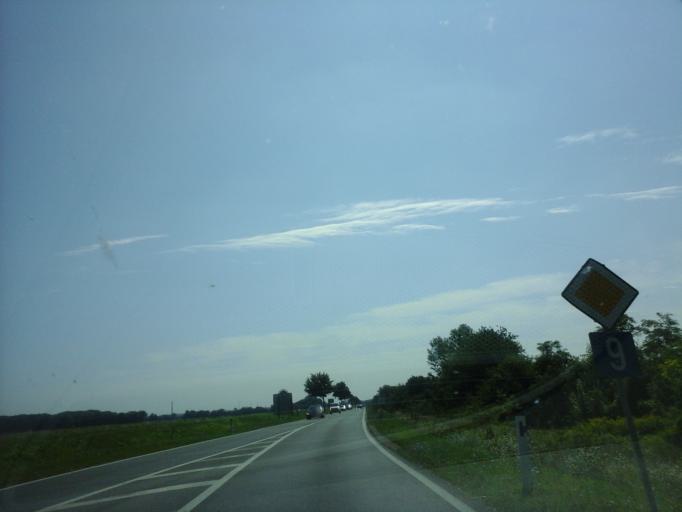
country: AT
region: Lower Austria
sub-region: Politischer Bezirk Bruck an der Leitha
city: Berg
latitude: 48.1266
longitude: 17.0309
